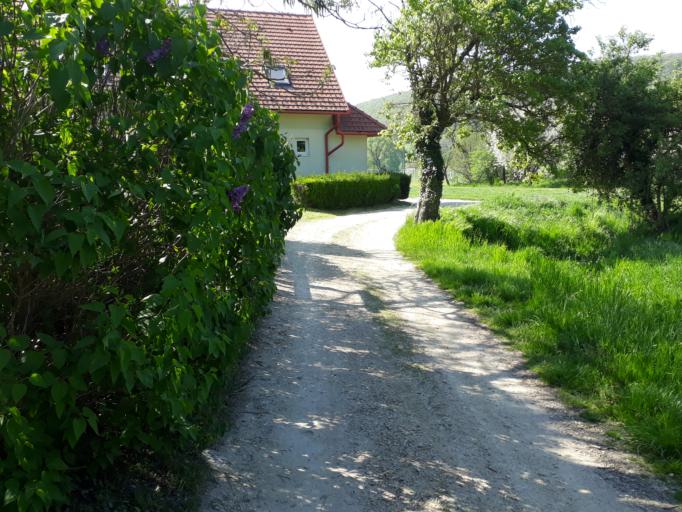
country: HU
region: Veszprem
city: Zanka
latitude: 46.9125
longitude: 17.6726
